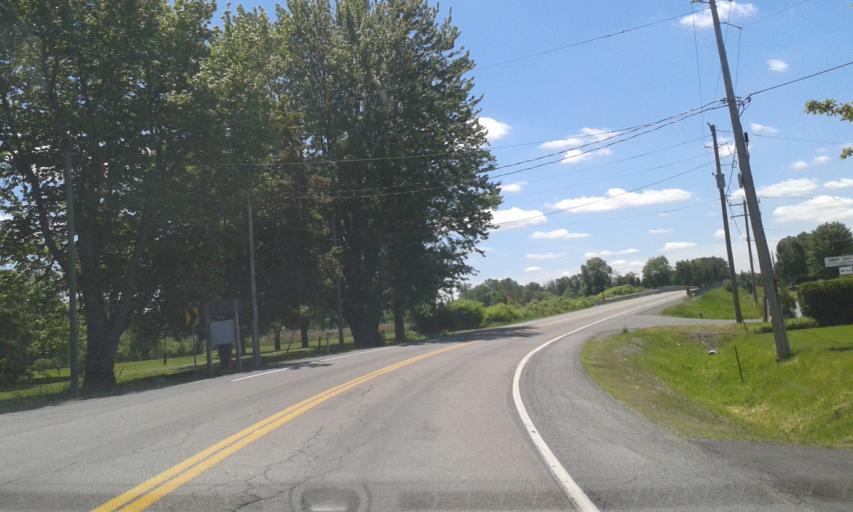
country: CA
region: Ontario
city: Cornwall
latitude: 45.1293
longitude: -74.4914
